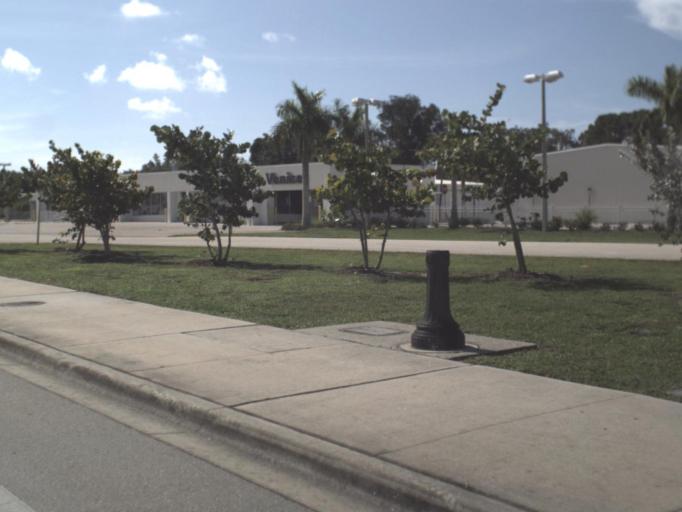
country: US
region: Florida
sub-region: Sarasota County
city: Venice Gardens
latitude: 27.0776
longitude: -82.4285
